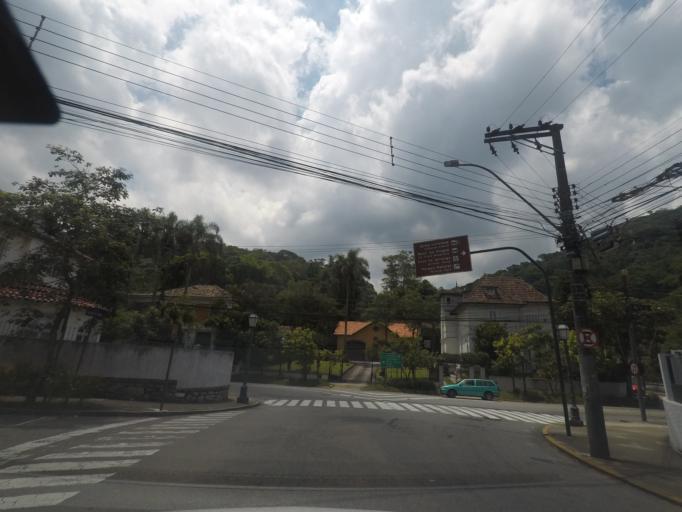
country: BR
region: Rio de Janeiro
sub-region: Petropolis
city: Petropolis
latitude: -22.5051
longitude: -43.1782
